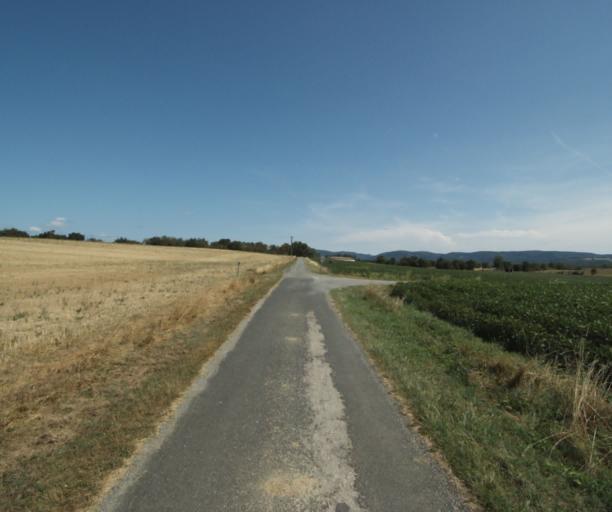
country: FR
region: Midi-Pyrenees
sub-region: Departement de la Haute-Garonne
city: Revel
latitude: 43.4871
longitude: 1.9985
